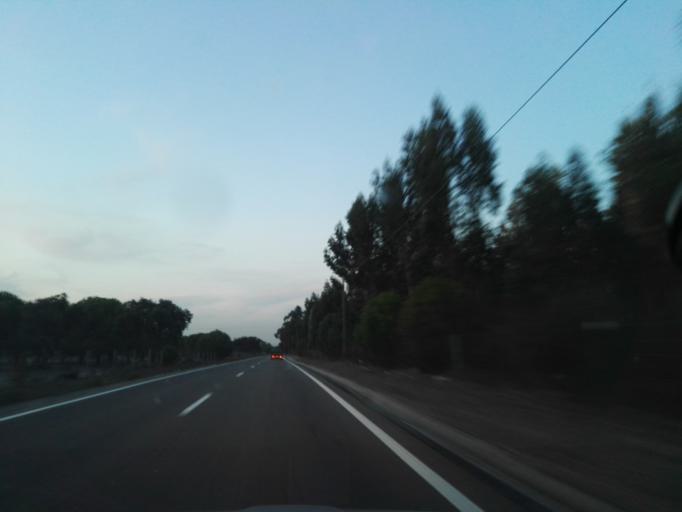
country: PT
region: Santarem
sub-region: Benavente
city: Benavente
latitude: 38.9247
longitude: -8.7756
